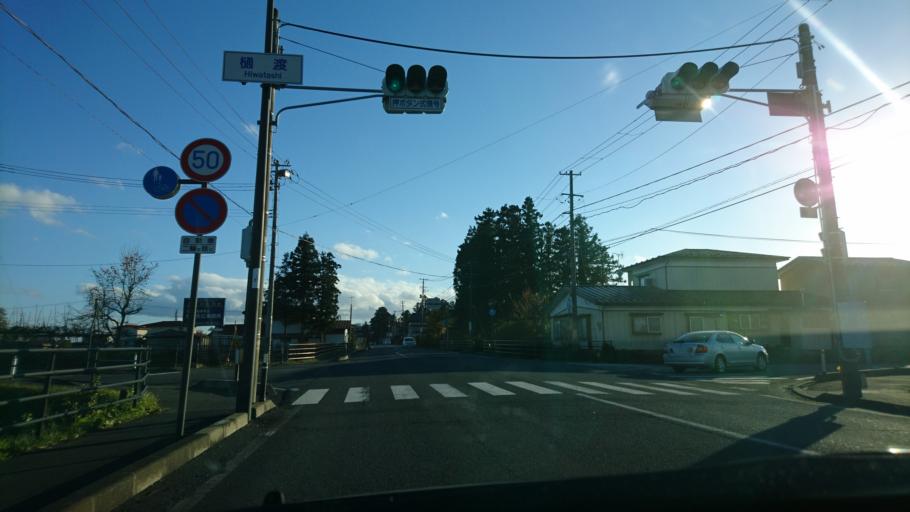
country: JP
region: Iwate
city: Ichinoseki
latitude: 38.9805
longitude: 141.1164
